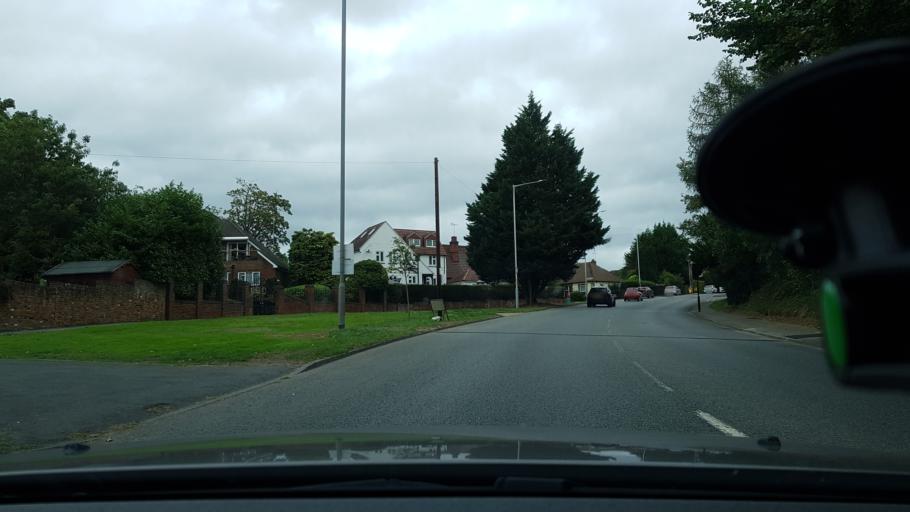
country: GB
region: England
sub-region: Greater London
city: Ruislip
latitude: 51.6062
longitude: -0.4247
